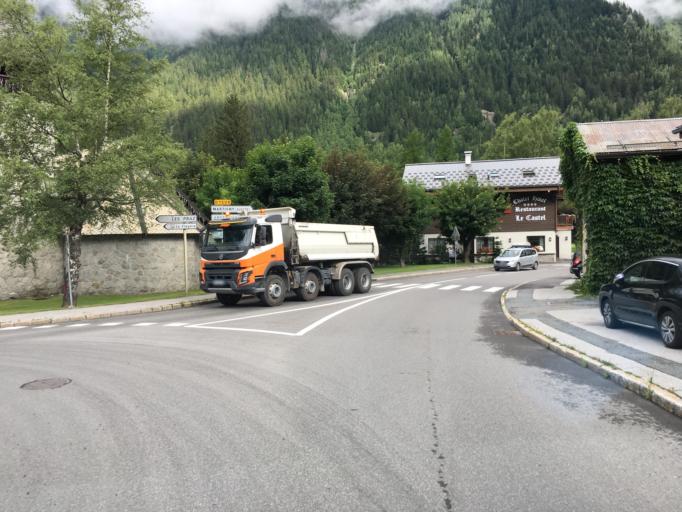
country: FR
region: Rhone-Alpes
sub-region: Departement de la Haute-Savoie
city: Chamonix-Mont-Blanc
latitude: 45.9405
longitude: 6.8878
